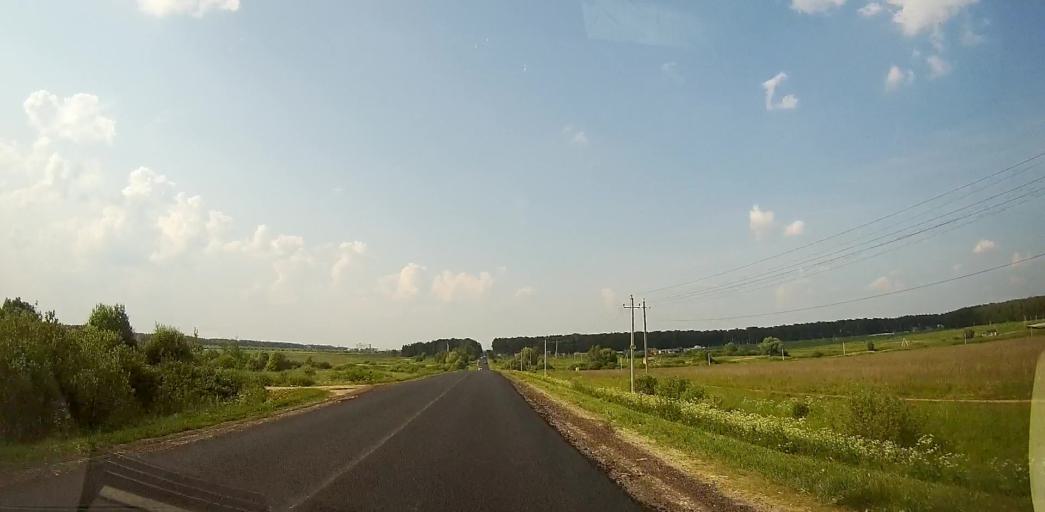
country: RU
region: Moskovskaya
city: Il'inskoye
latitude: 55.2258
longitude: 37.9253
